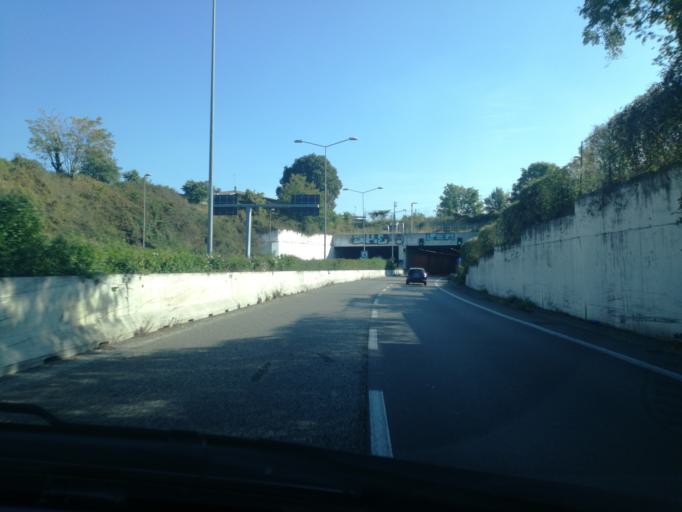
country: IT
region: Lombardy
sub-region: Provincia di Bergamo
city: Presezzo
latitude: 45.6845
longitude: 9.5719
